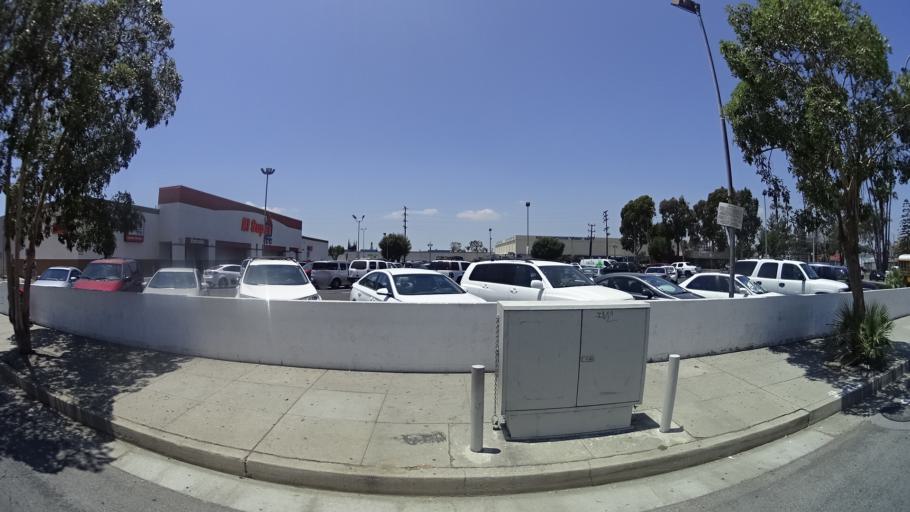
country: US
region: California
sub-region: Los Angeles County
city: Van Nuys
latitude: 34.2269
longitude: -118.4503
